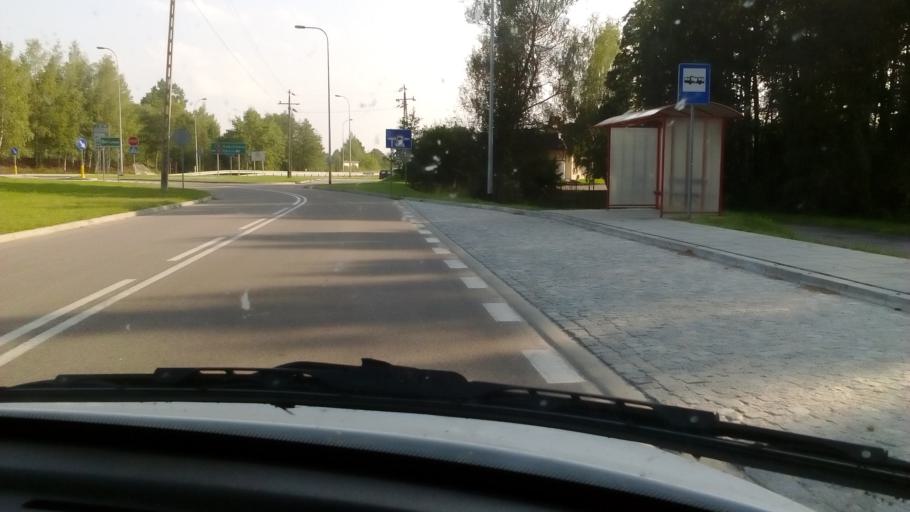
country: LT
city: Lazdijai
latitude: 54.1593
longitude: 23.4723
